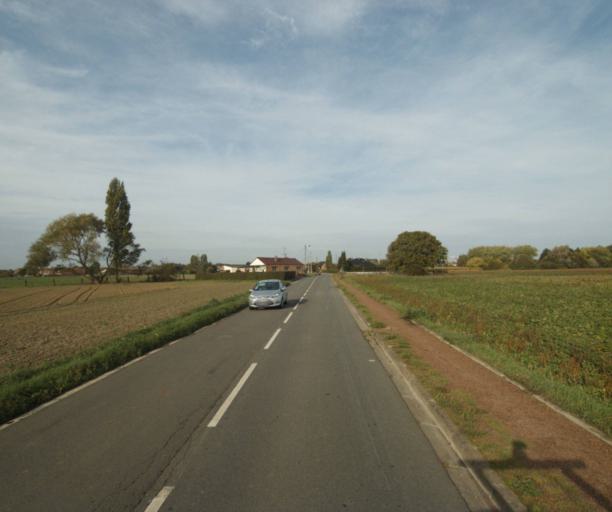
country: FR
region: Nord-Pas-de-Calais
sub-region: Departement du Nord
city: Sainghin-en-Weppes
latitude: 50.5630
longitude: 2.9114
